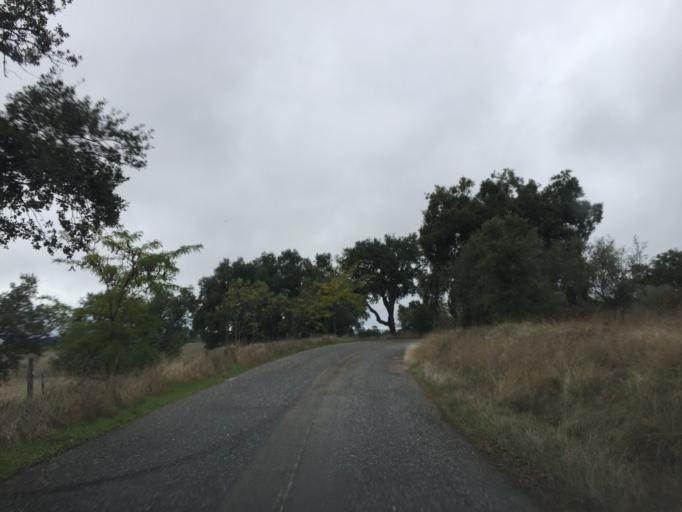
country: PT
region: Portalegre
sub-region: Alter do Chao
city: Alter do Chao
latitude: 39.2346
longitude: -7.6528
